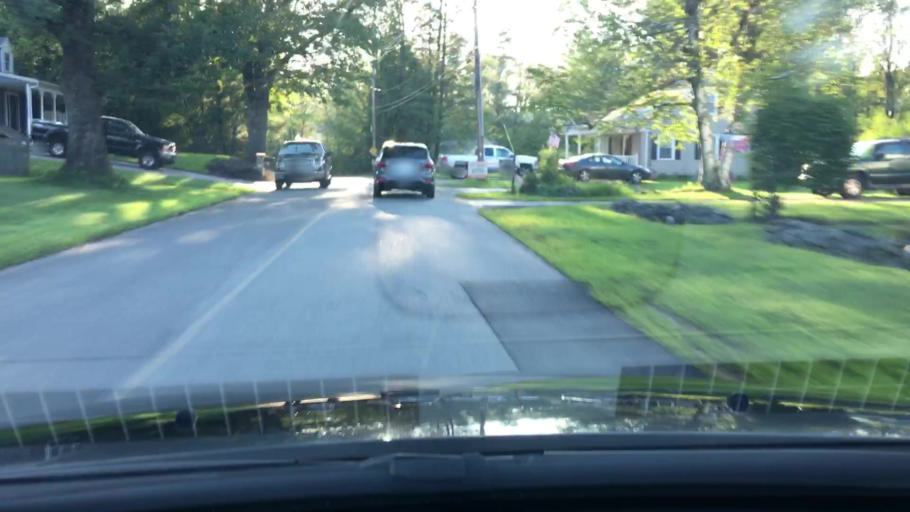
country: US
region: Massachusetts
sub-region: Worcester County
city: West Boylston
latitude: 42.3488
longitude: -71.7813
